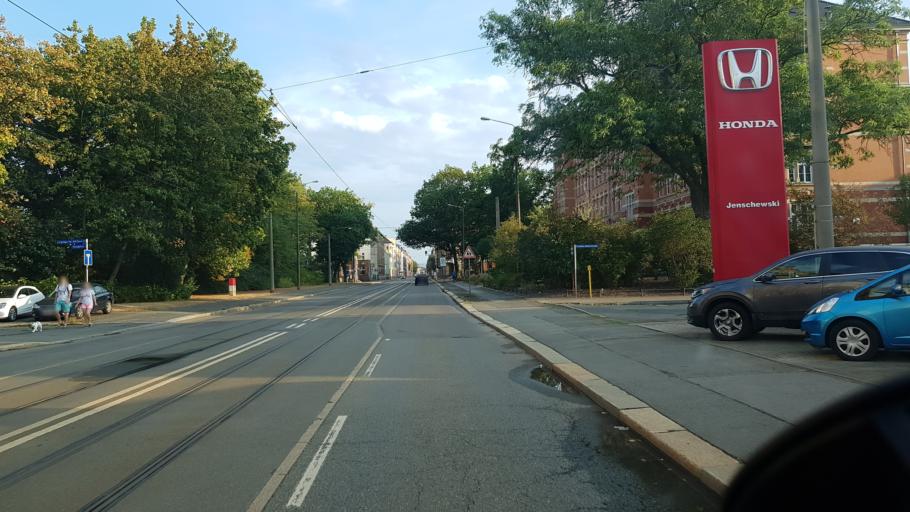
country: DE
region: Saxony
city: Zwickau
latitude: 50.7355
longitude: 12.4905
